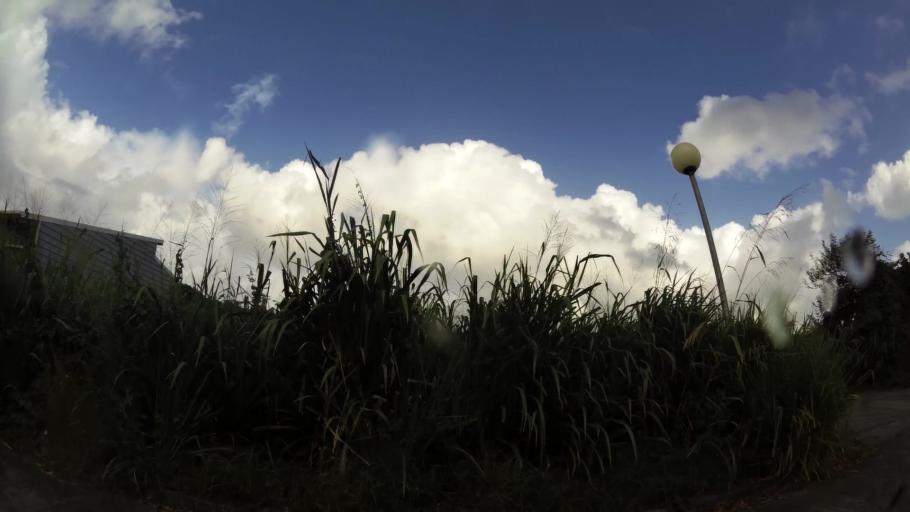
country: MQ
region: Martinique
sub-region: Martinique
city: Sainte-Luce
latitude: 14.4951
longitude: -60.9763
